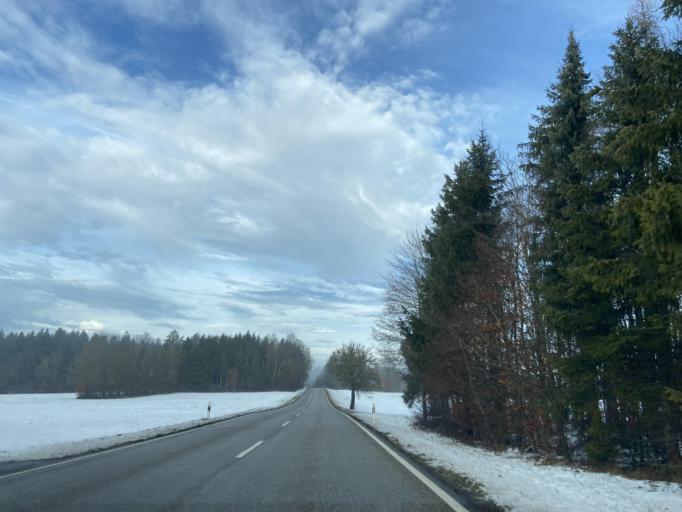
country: DE
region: Baden-Wuerttemberg
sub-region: Tuebingen Region
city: Hettingen
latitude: 48.2279
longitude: 9.2868
